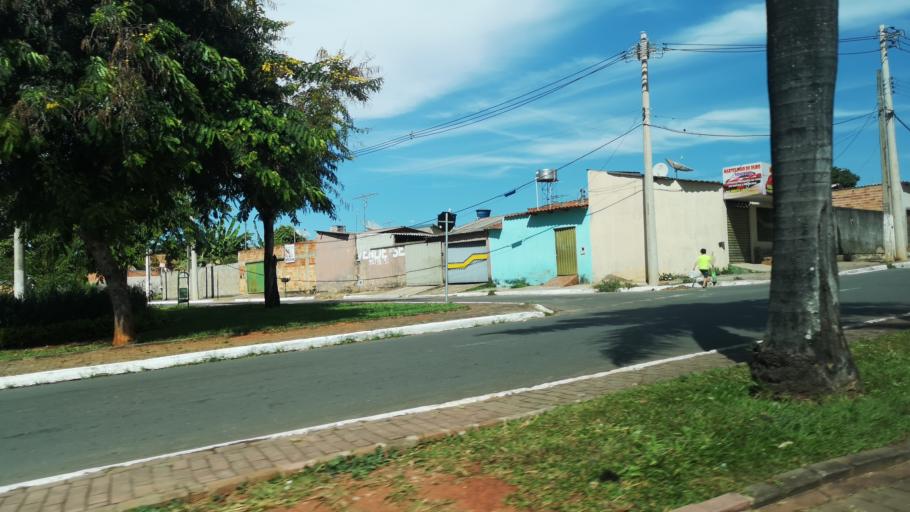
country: BR
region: Goias
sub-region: Senador Canedo
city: Senador Canedo
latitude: -16.6923
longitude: -49.0971
